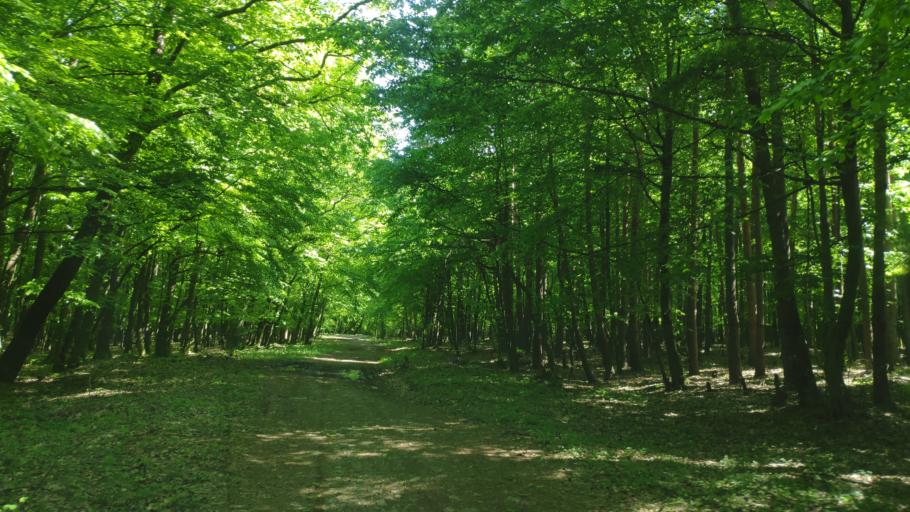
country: SK
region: Kosicky
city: Secovce
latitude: 48.7062
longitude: 21.5850
